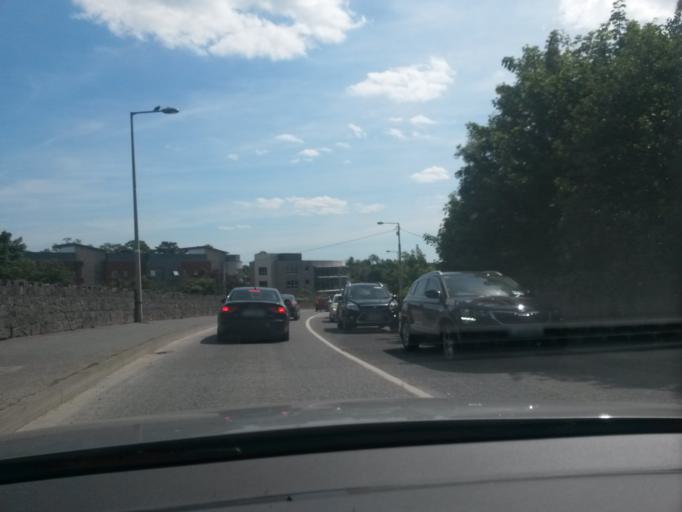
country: IE
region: Leinster
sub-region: Kildare
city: Sallins
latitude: 53.2467
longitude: -6.6656
